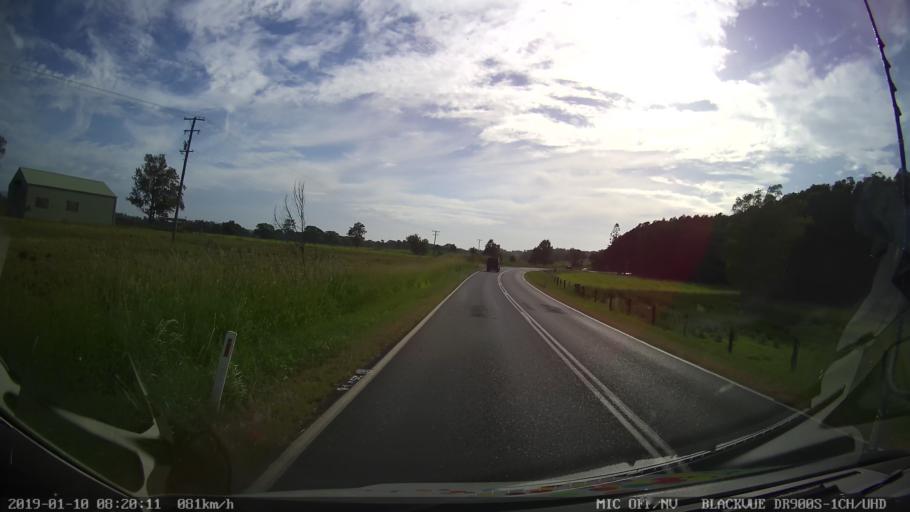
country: AU
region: New South Wales
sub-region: Bellingen
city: Bellingen
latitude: -30.4657
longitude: 152.9789
